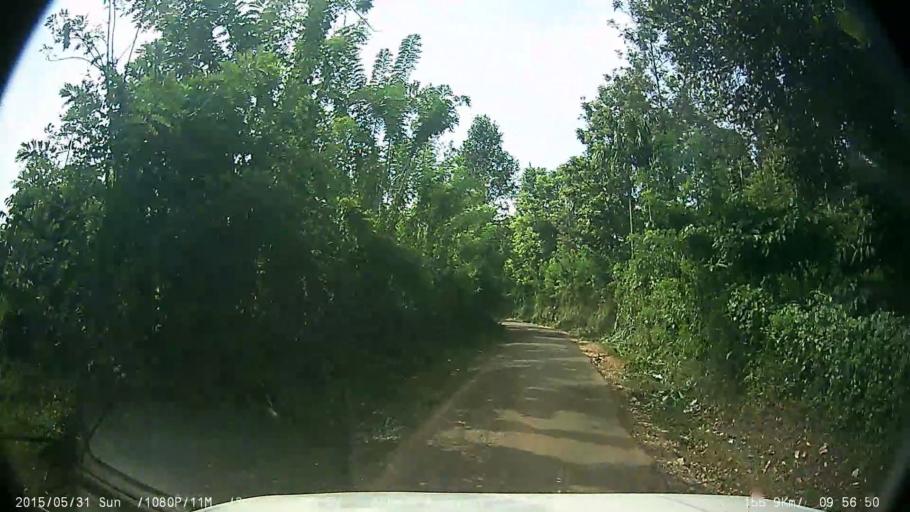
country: IN
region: Kerala
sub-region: Wayanad
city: Kalpetta
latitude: 11.5966
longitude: 76.0574
